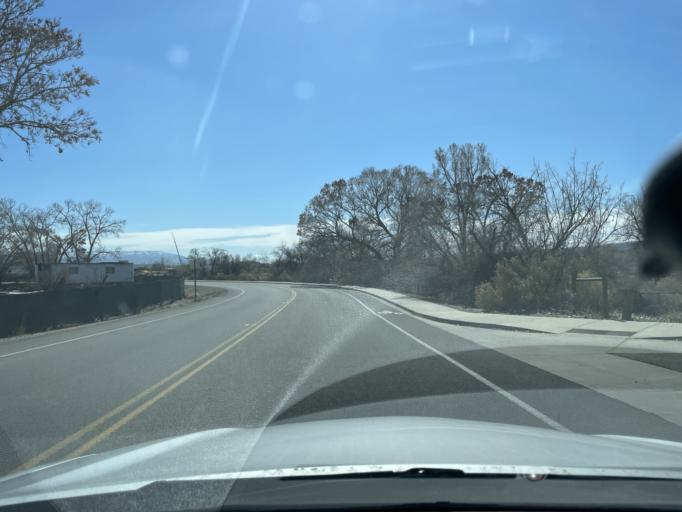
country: US
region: Colorado
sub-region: Mesa County
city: Redlands
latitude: 39.0895
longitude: -108.6113
